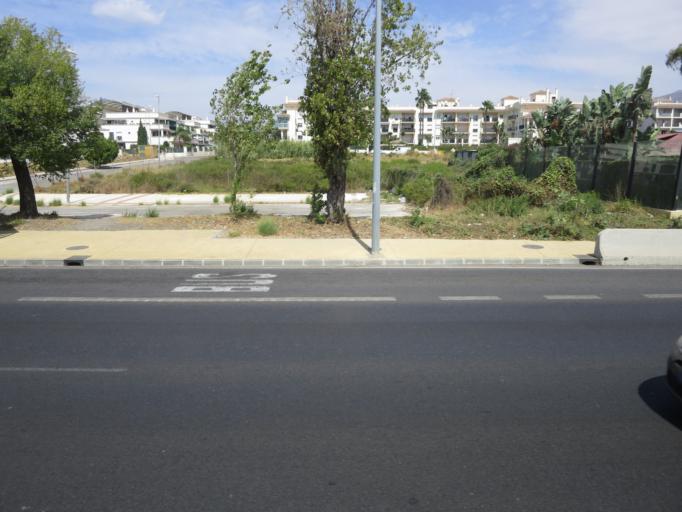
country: ES
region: Andalusia
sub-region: Provincia de Malaga
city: Benahavis
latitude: 36.4870
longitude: -4.9678
